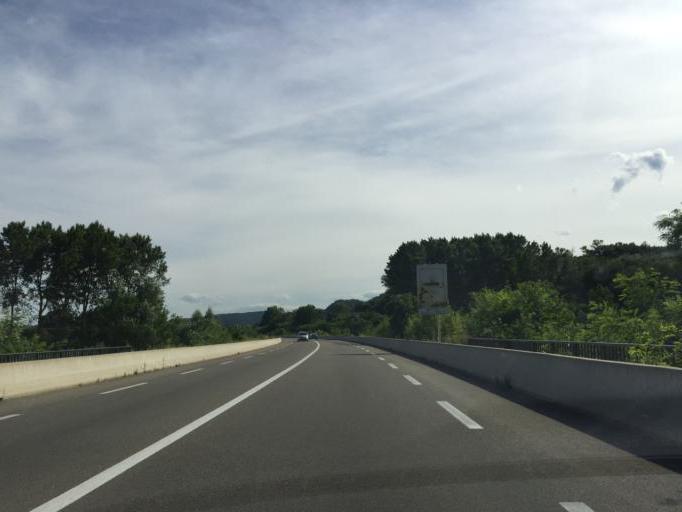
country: FR
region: Rhone-Alpes
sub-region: Departement de l'Ardeche
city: Rochemaure
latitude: 44.5765
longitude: 4.6997
